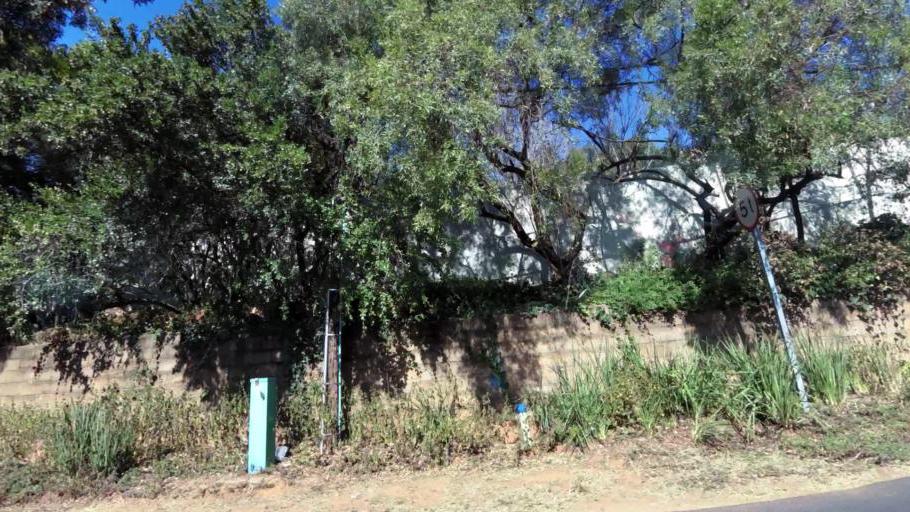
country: ZA
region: Gauteng
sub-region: City of Johannesburg Metropolitan Municipality
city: Roodepoort
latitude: -26.1432
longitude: 27.9668
